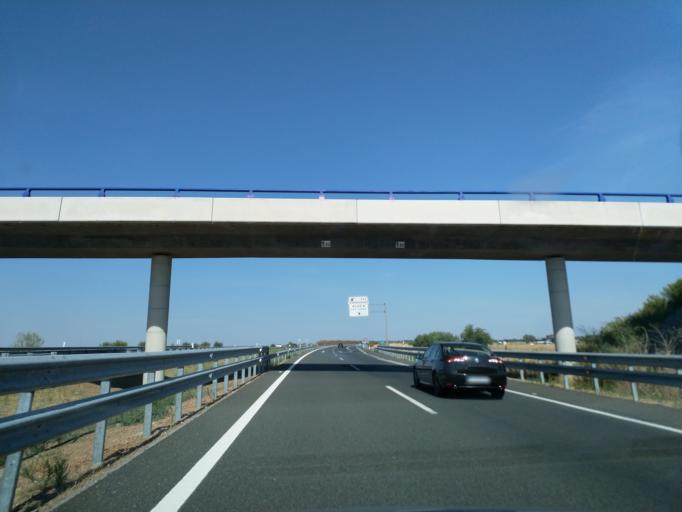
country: ES
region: Extremadura
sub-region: Provincia de Caceres
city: Aldea del Cano
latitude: 39.2841
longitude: -6.3286
